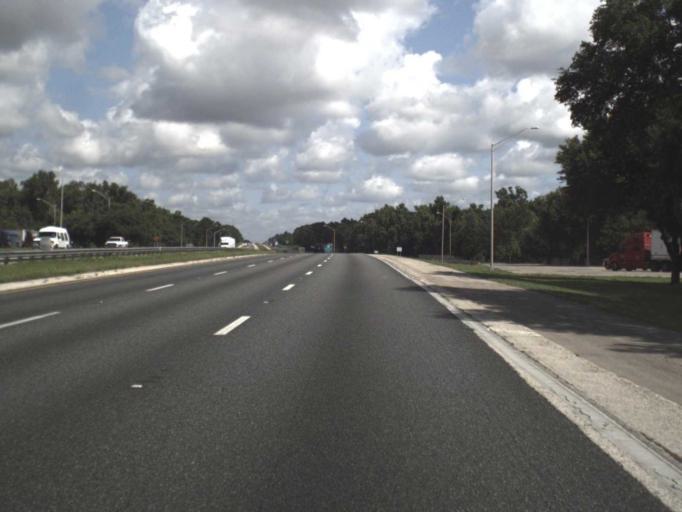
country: US
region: Florida
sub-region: Alachua County
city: Gainesville
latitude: 29.5893
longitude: -82.3620
